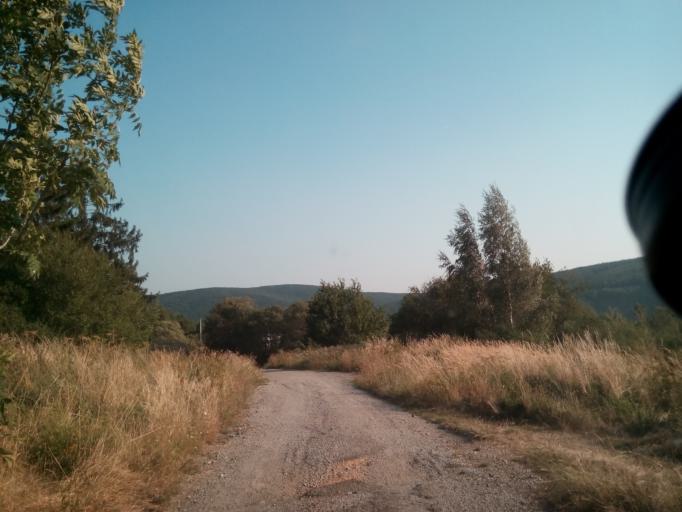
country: SK
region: Kosicky
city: Moldava nad Bodvou
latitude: 48.7302
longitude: 21.1004
